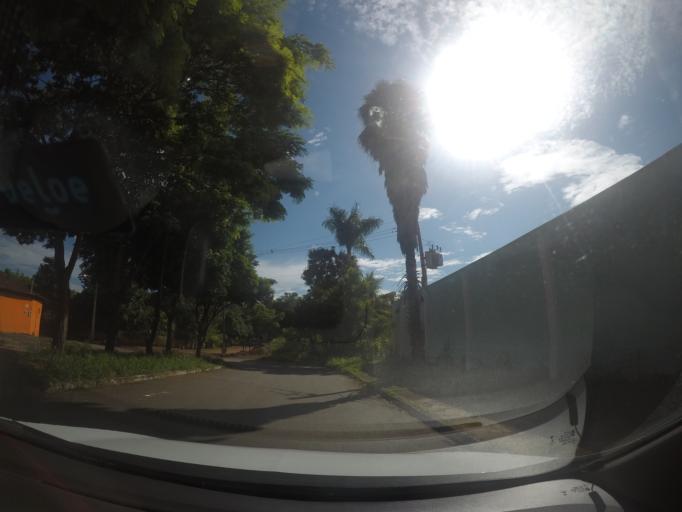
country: BR
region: Goias
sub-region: Goiania
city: Goiania
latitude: -16.6608
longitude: -49.2054
